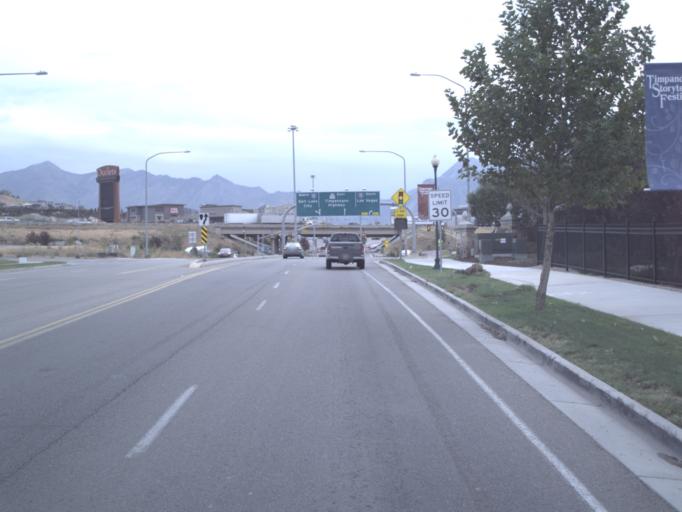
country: US
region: Utah
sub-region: Utah County
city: Lehi
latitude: 40.4312
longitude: -111.8945
